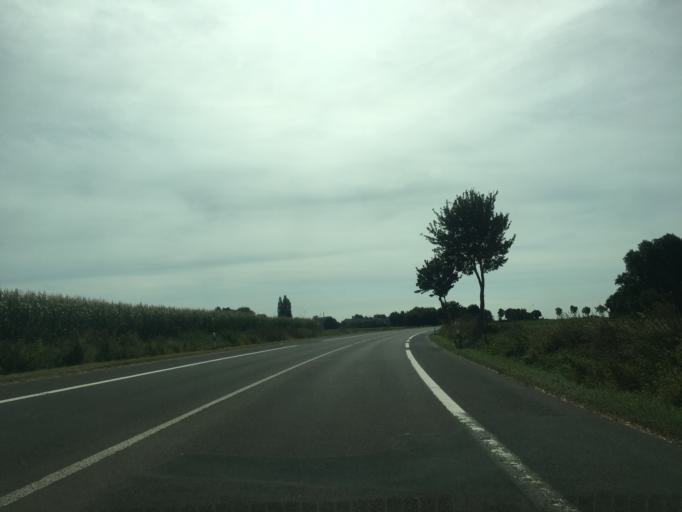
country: DE
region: North Rhine-Westphalia
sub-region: Regierungsbezirk Koln
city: Titz
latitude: 51.0495
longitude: 6.3928
